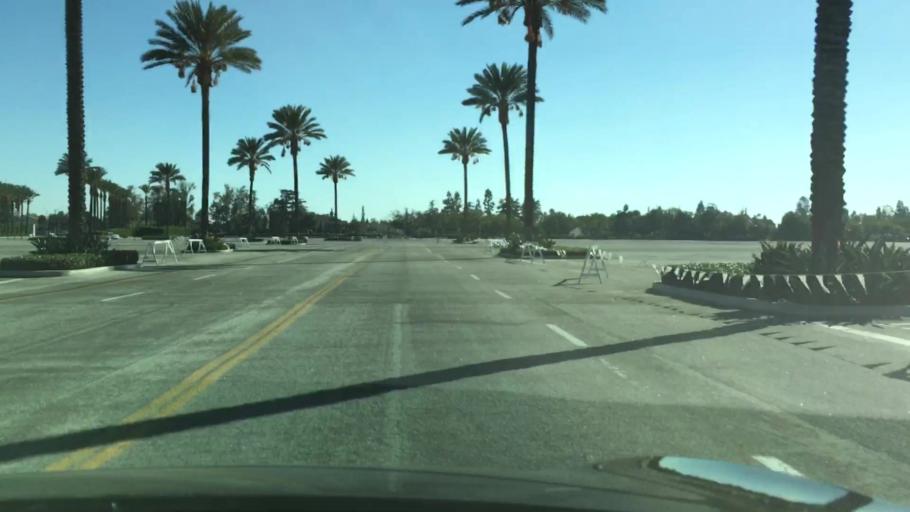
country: US
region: California
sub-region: Los Angeles County
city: Arcadia
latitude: 34.1352
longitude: -118.0461
